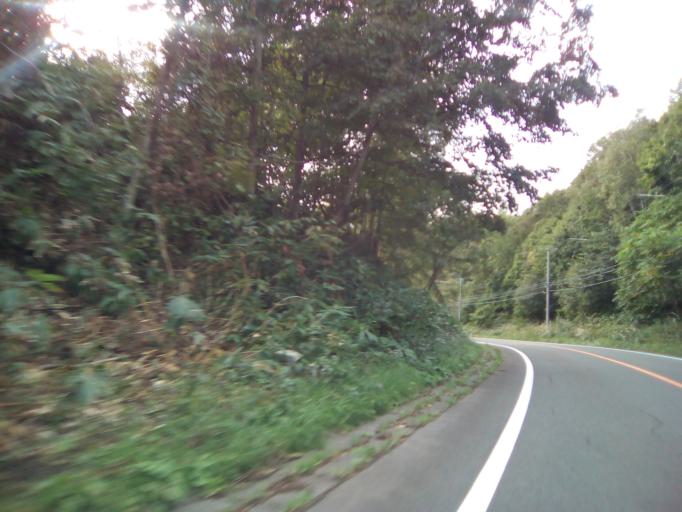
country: JP
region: Hokkaido
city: Date
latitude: 42.6620
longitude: 140.8303
